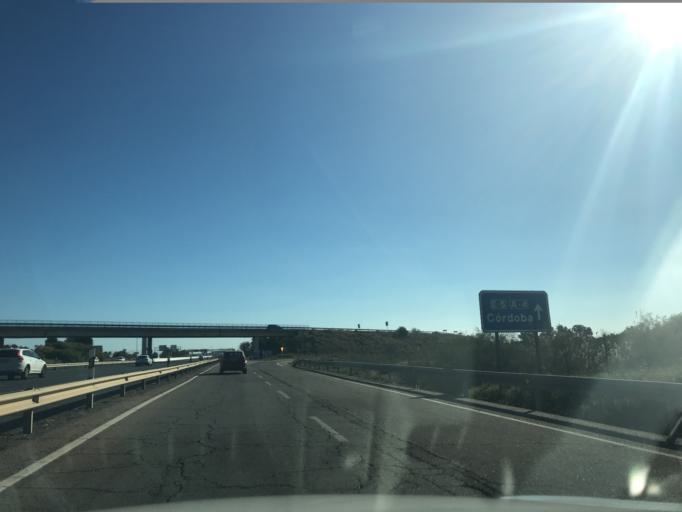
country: ES
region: Andalusia
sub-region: Provincia de Sevilla
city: Sevilla
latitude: 37.4156
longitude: -5.9261
